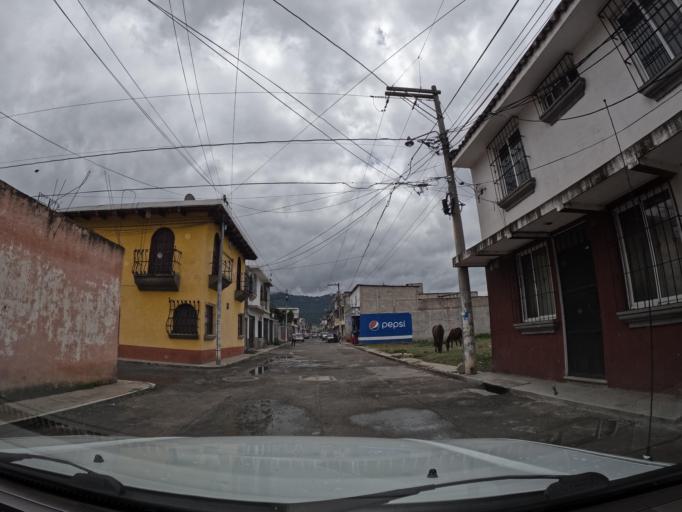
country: GT
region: Sacatepequez
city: Jocotenango
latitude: 14.5782
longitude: -90.7489
